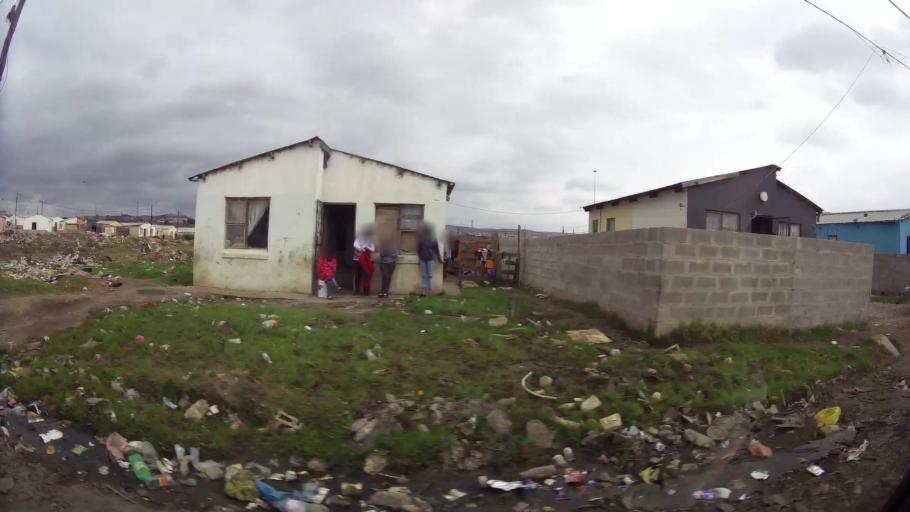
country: ZA
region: Eastern Cape
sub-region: Nelson Mandela Bay Metropolitan Municipality
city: Port Elizabeth
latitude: -33.8875
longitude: 25.5538
